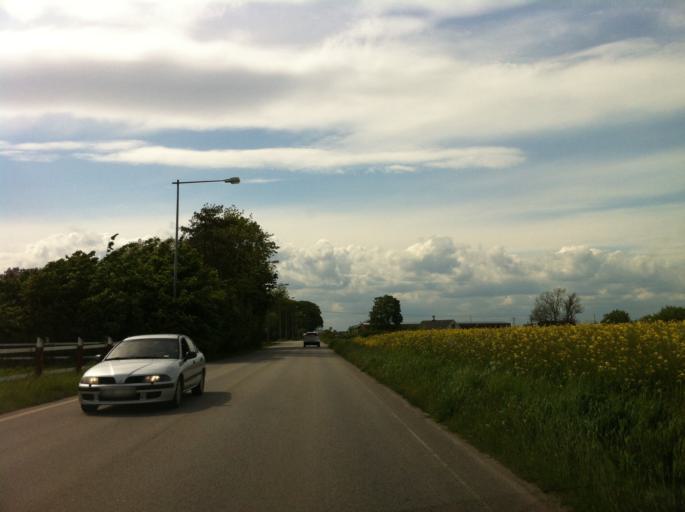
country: SE
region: Skane
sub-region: Landskrona
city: Asmundtorp
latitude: 55.8616
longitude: 12.8954
